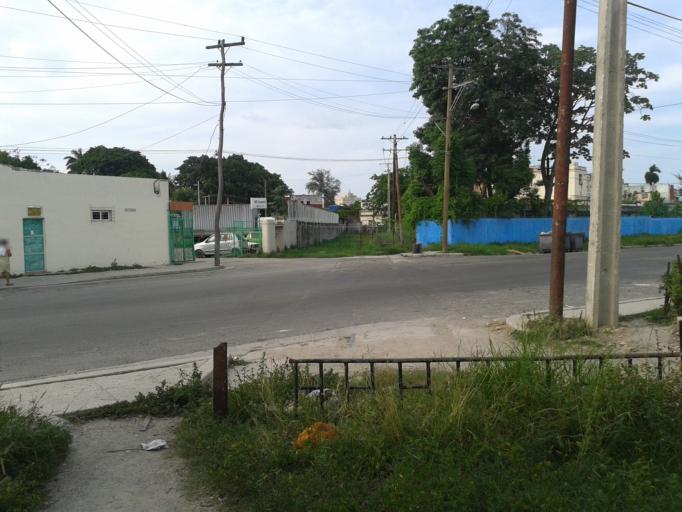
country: CU
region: La Habana
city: Havana
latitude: 23.1231
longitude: -82.3762
